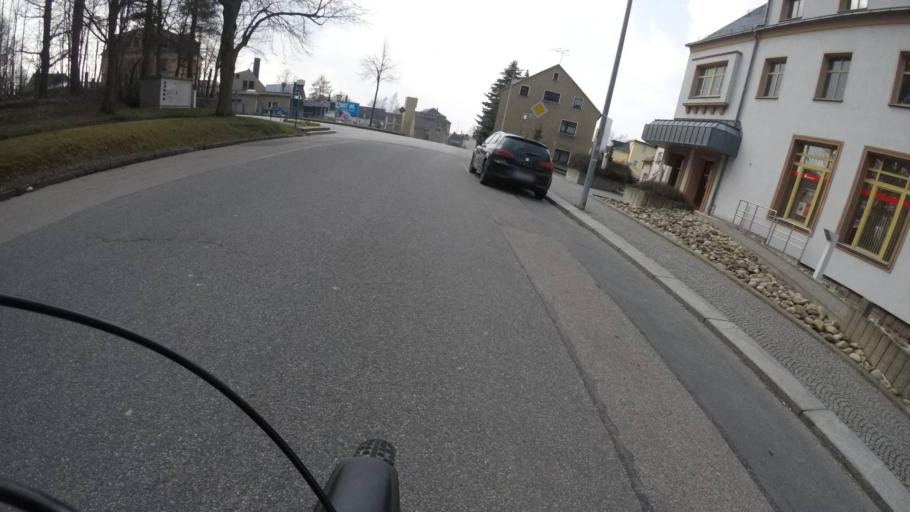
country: DE
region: Saxony
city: Limbach-Oberfrohna
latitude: 50.8647
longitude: 12.7441
